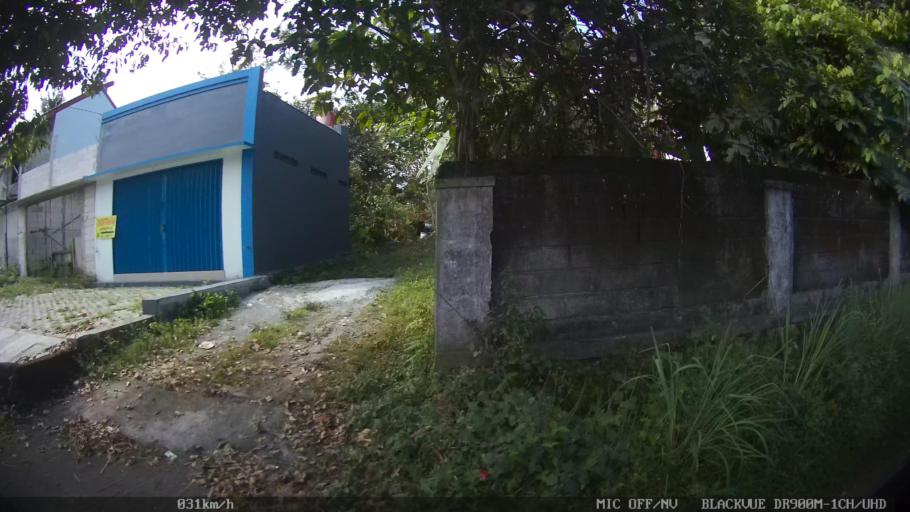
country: ID
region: Daerah Istimewa Yogyakarta
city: Depok
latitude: -7.7284
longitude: 110.4161
